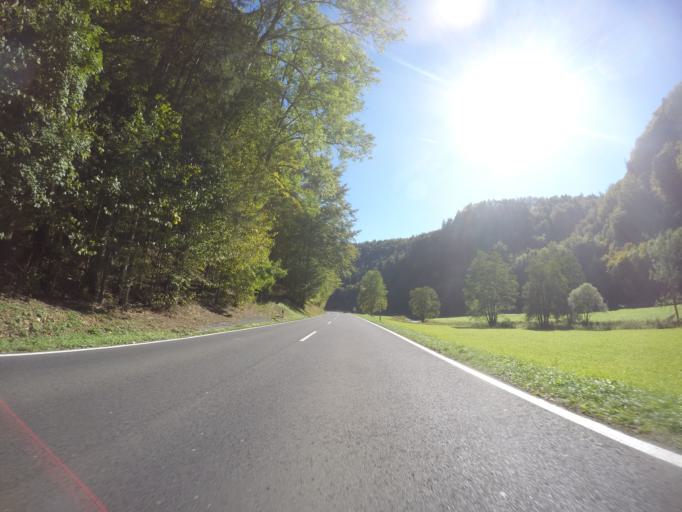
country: DE
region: Bavaria
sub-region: Upper Franconia
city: Gossweinstein
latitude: 49.7756
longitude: 11.2963
